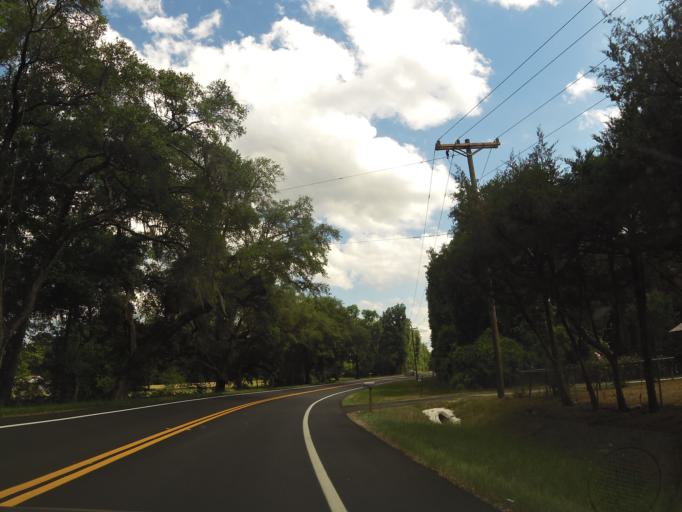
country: US
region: Florida
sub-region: Clay County
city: Keystone Heights
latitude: 29.7968
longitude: -81.9141
